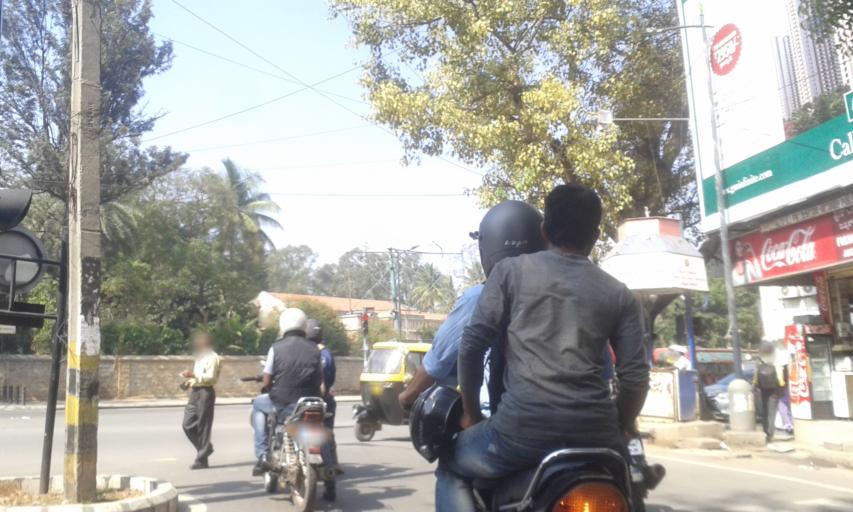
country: IN
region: Karnataka
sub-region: Bangalore Urban
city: Bangalore
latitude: 12.9682
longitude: 77.6065
